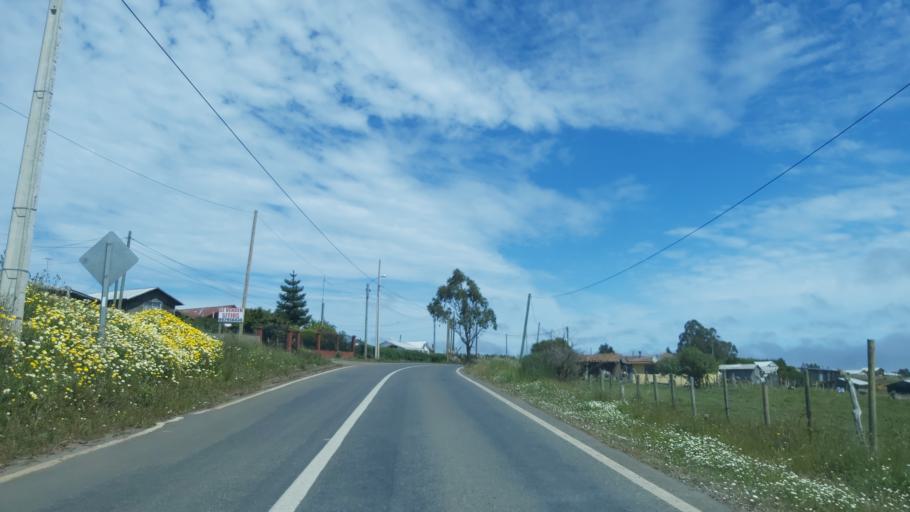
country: CL
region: Maule
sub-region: Provincia de Talca
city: Constitucion
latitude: -35.5766
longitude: -72.6022
